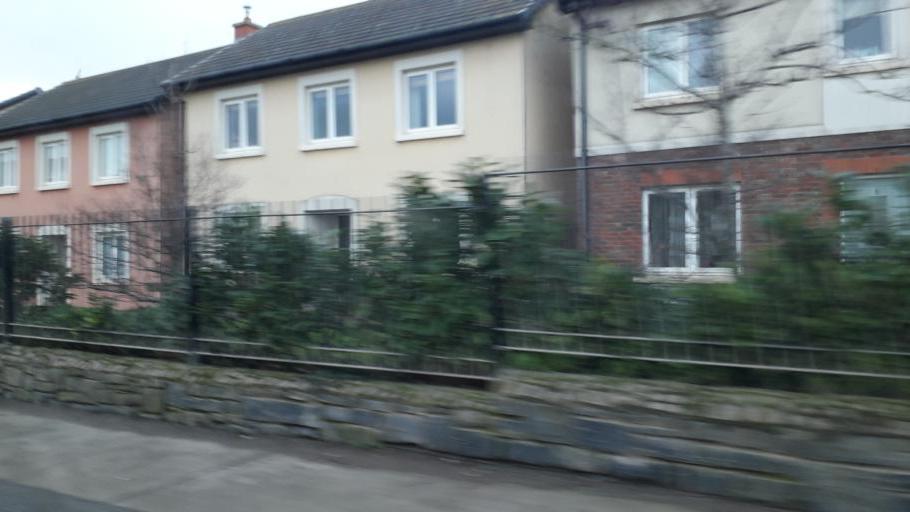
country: IE
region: Leinster
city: An Ros
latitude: 53.5269
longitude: -6.0912
